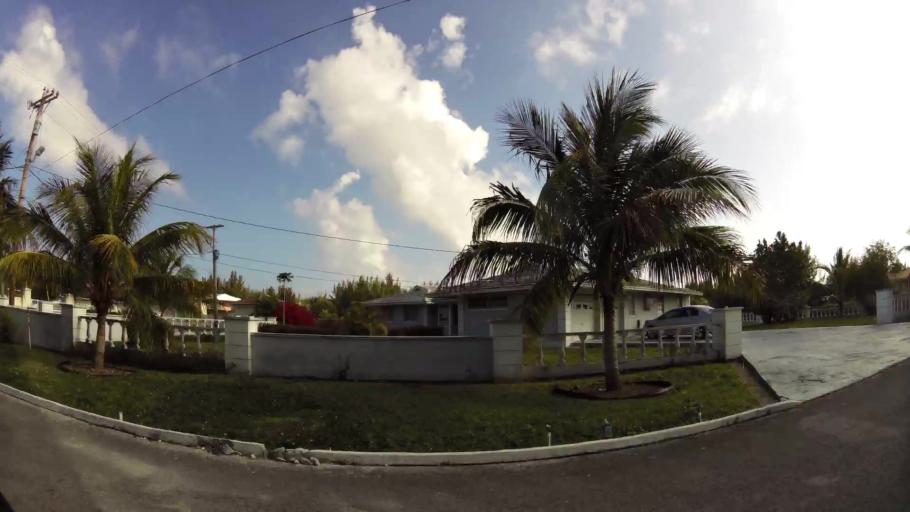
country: BS
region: Freeport
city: Lucaya
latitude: 26.5038
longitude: -78.6591
